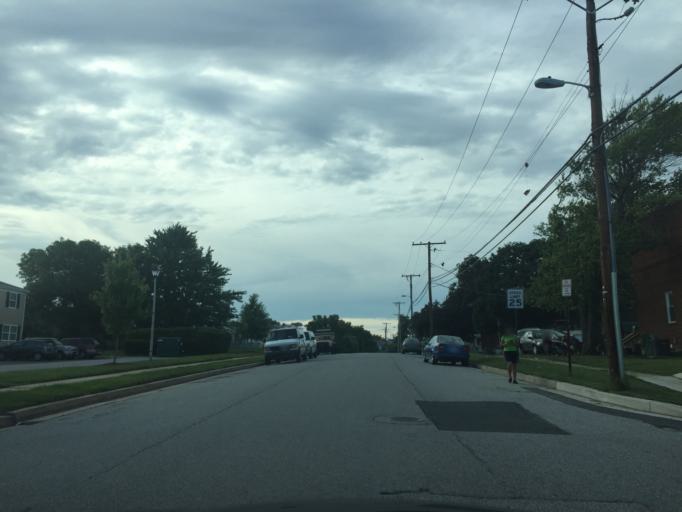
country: US
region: Maryland
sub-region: Baltimore County
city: Middle River
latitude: 39.3372
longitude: -76.4446
